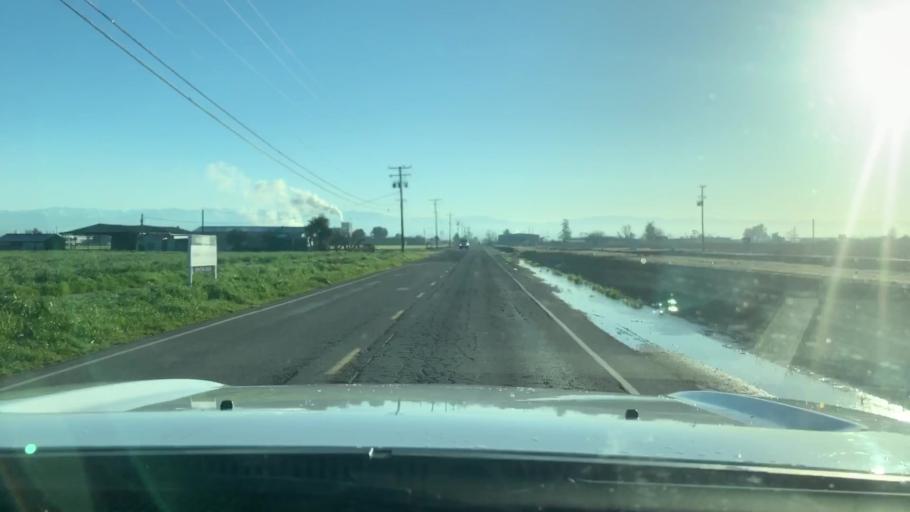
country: US
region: California
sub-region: Tulare County
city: Tulare
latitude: 36.1820
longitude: -119.3504
